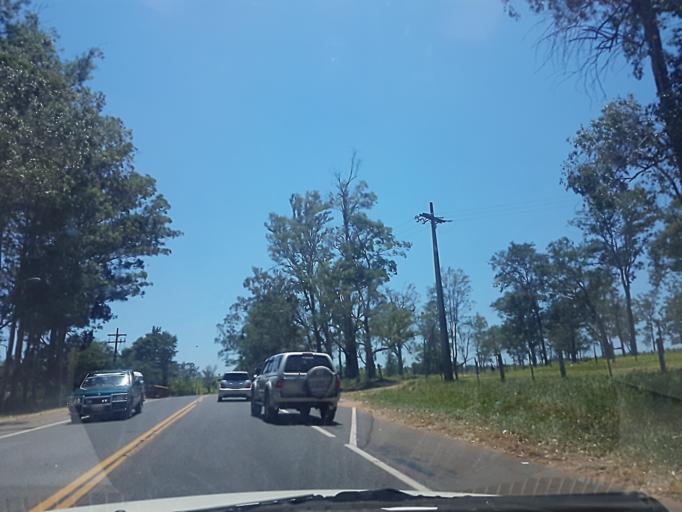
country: PY
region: Cordillera
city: Caacupe
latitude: -25.3894
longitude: -57.0649
